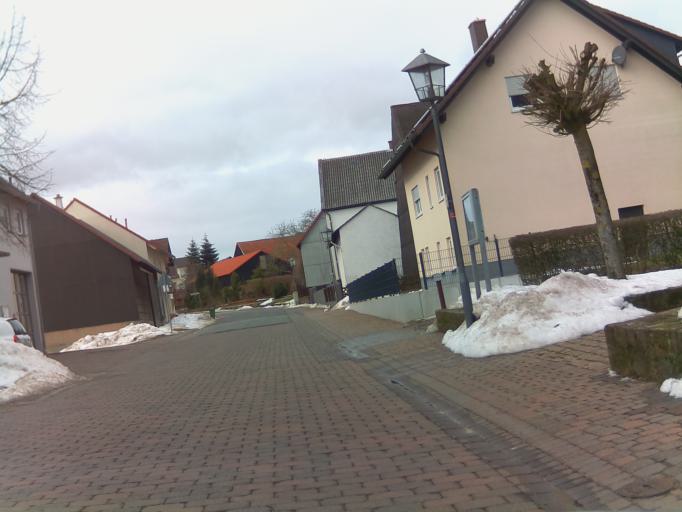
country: DE
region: Hesse
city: Michelstadt
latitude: 49.6539
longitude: 9.0797
